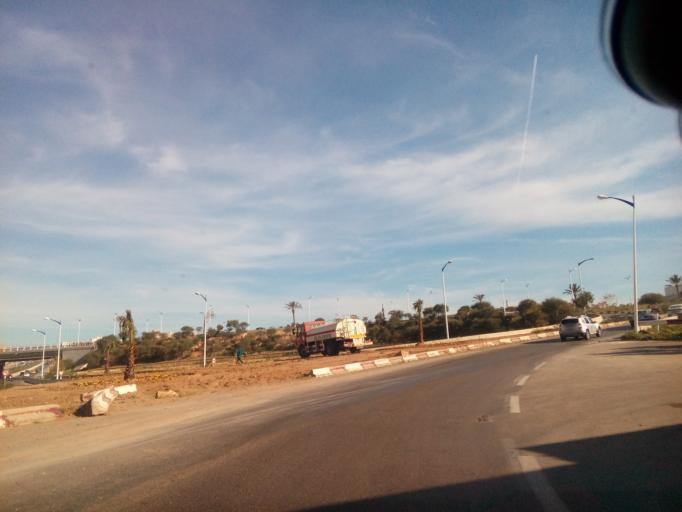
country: DZ
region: Mostaganem
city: Mostaganem
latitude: 35.9121
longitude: 0.0734
